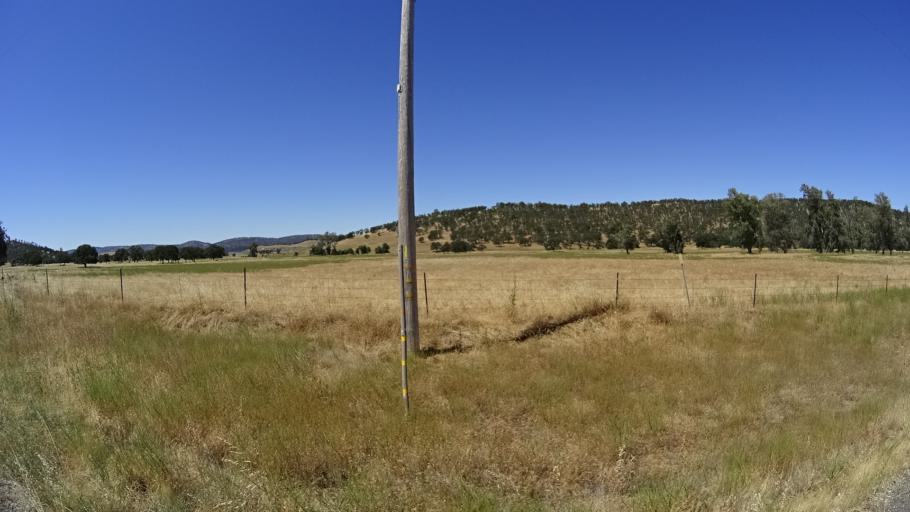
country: US
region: California
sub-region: Calaveras County
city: Copperopolis
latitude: 38.0155
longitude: -120.6750
